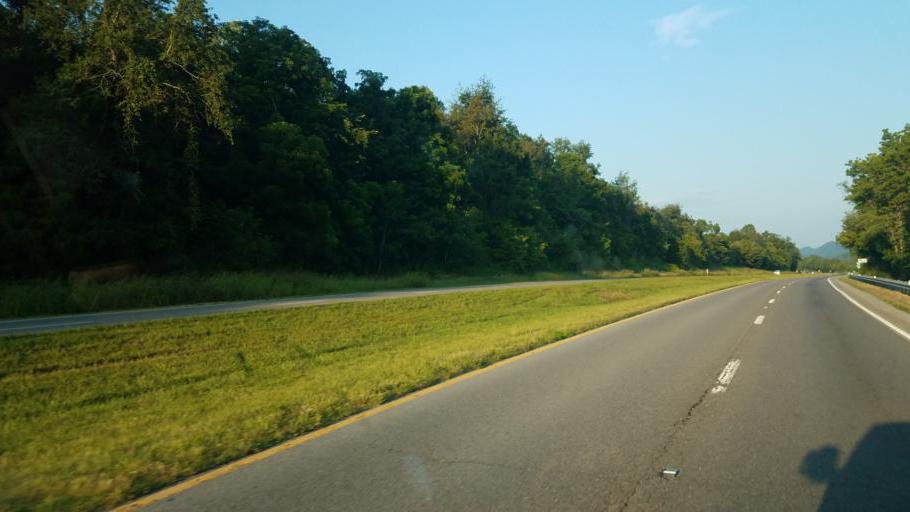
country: US
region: Tennessee
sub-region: Hawkins County
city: Mount Carmel
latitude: 36.6415
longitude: -82.6952
